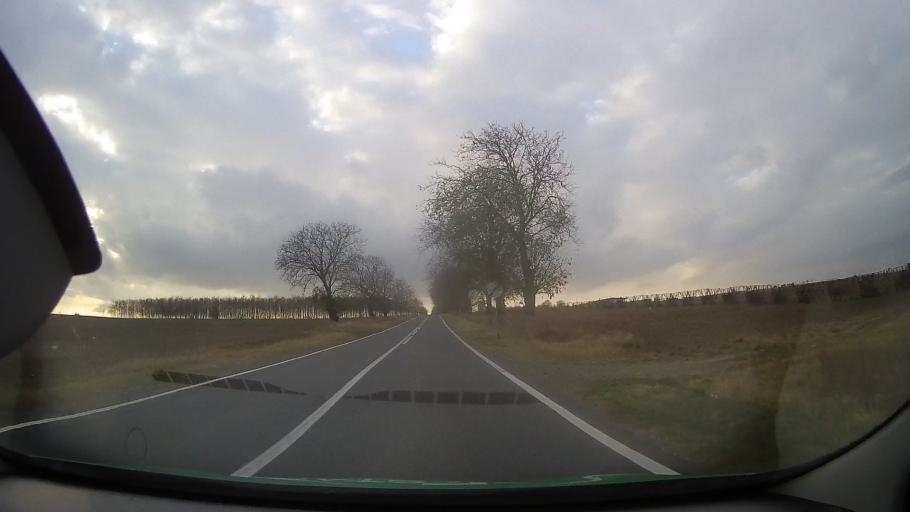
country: RO
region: Constanta
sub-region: Comuna Adamclisi
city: Adamclisi
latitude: 44.0877
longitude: 27.9773
